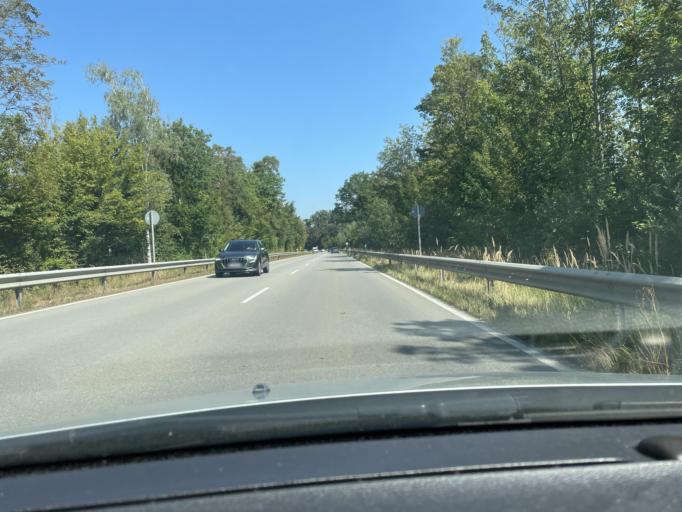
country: DE
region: Baden-Wuerttemberg
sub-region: Karlsruhe Region
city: Rheinmuenster
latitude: 48.7633
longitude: 8.0169
